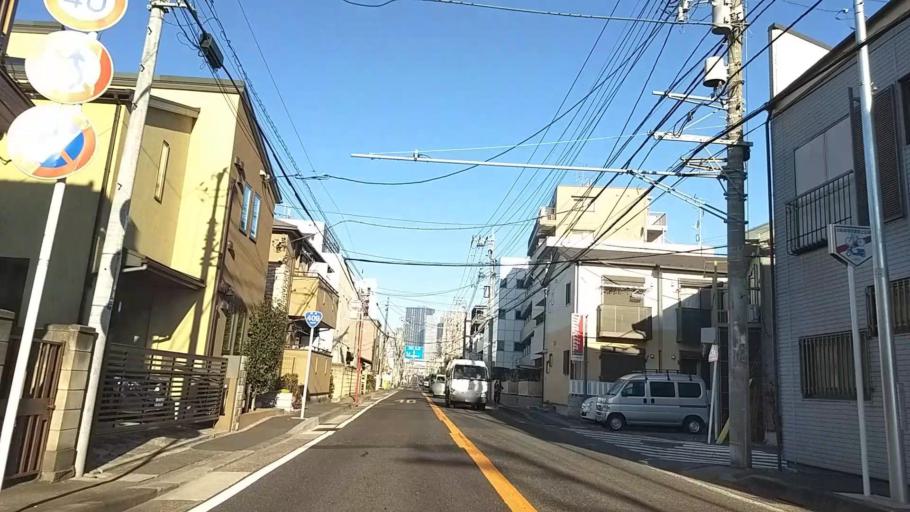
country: JP
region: Kanagawa
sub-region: Kawasaki-shi
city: Kawasaki
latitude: 35.5598
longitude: 139.6706
